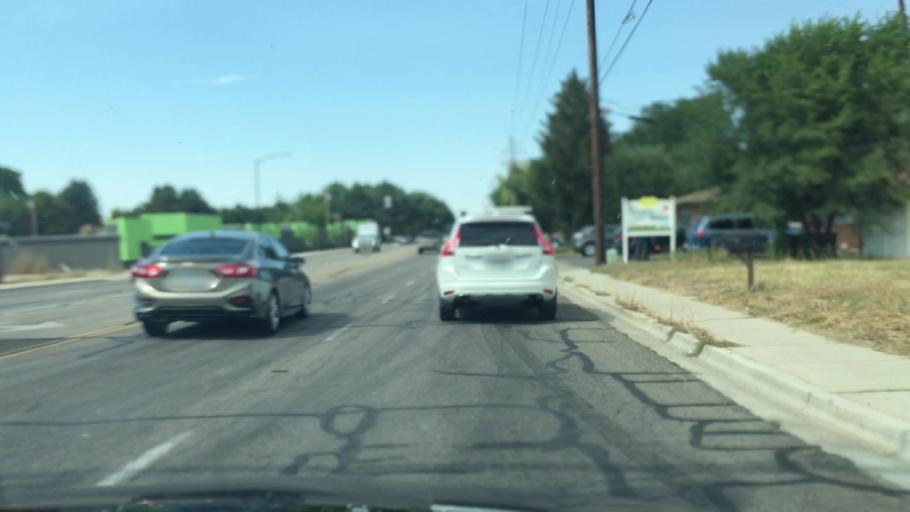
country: US
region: Idaho
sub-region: Ada County
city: Garden City
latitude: 43.6268
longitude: -116.2742
